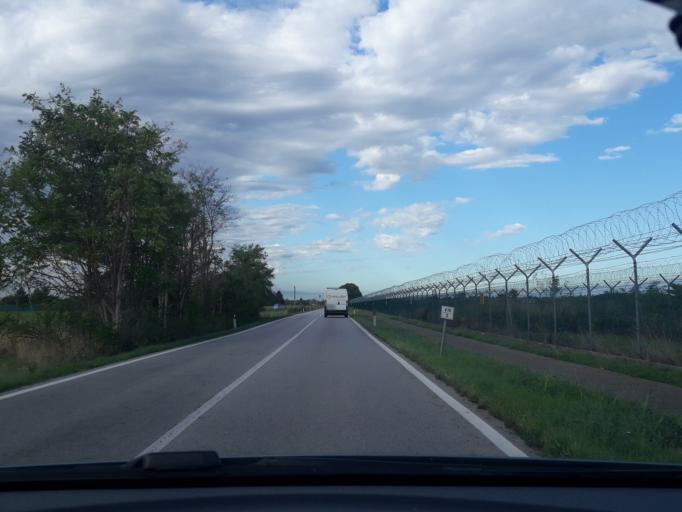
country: IT
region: Friuli Venezia Giulia
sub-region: Provincia di Udine
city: Pasian di Prato
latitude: 46.0225
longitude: 13.1833
